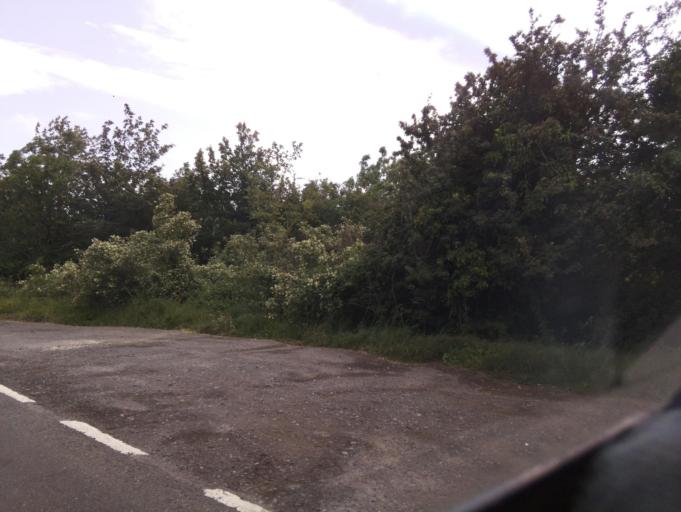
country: GB
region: Wales
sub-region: Vale of Glamorgan
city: Rhoose
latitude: 51.3980
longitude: -3.4107
